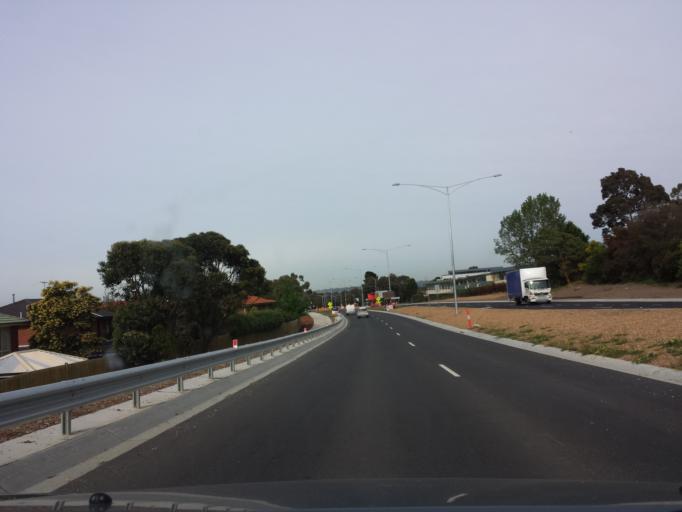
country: AU
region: Victoria
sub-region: Knox
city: Knoxfield
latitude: -37.8742
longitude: 145.2469
